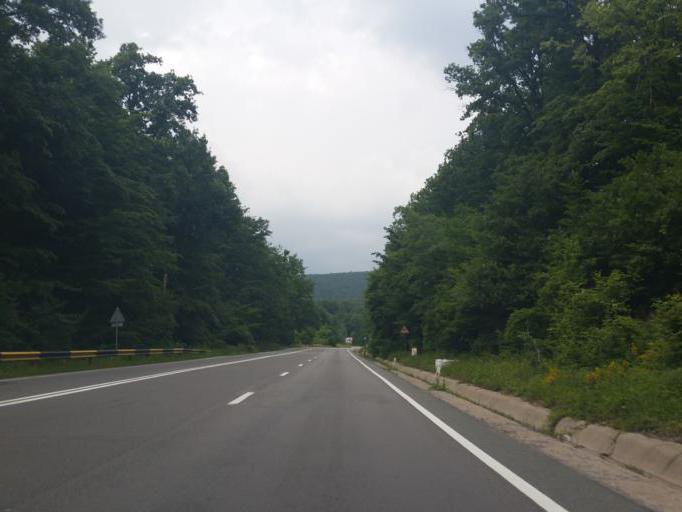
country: RO
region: Salaj
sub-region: Comuna Treznea
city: Treznea
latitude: 47.1397
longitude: 23.1172
